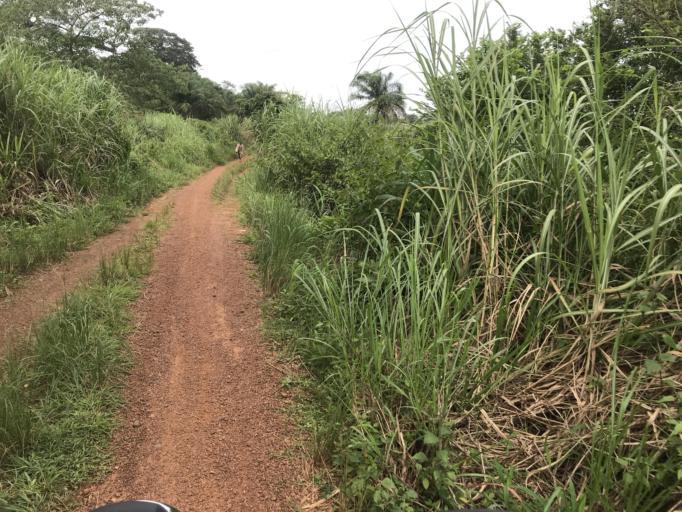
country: SL
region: Eastern Province
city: Buedu
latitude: 8.4693
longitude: -10.3311
